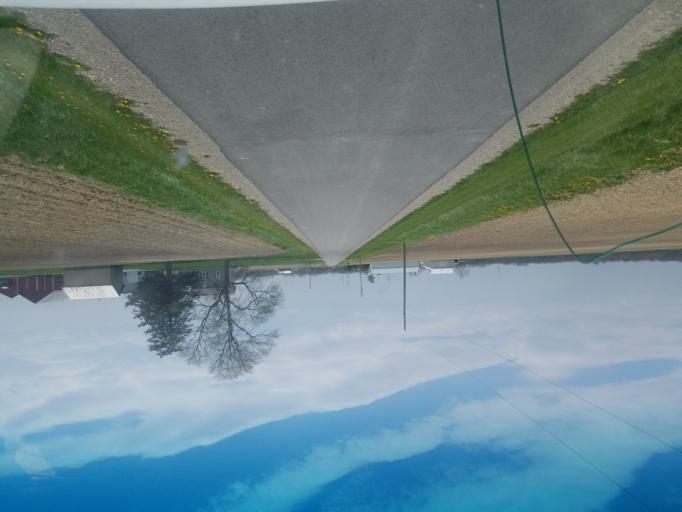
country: US
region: Ohio
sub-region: Wyandot County
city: Upper Sandusky
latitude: 40.7737
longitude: -83.3849
